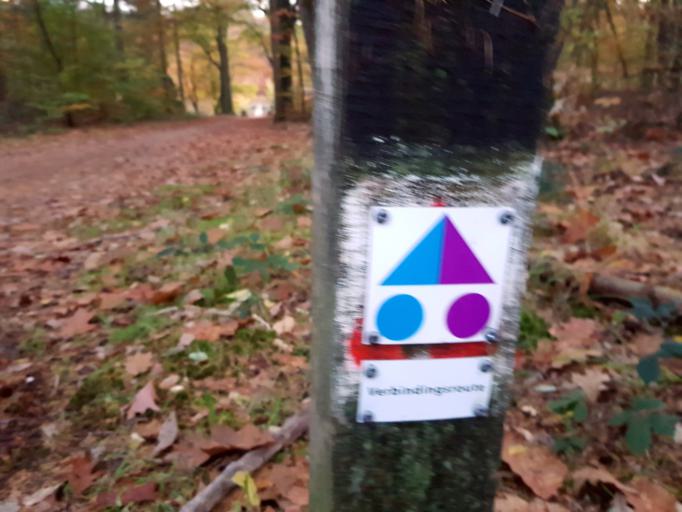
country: NL
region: Gelderland
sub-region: Gemeente Groesbeek
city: Groesbeek
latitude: 51.7769
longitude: 5.9096
